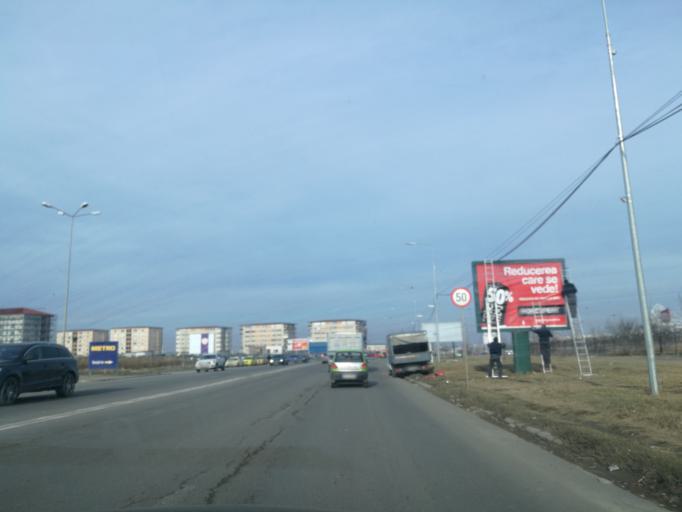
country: RO
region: Constanta
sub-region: Municipiul Constanta
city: Palazu Mare
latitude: 44.1972
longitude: 28.6050
